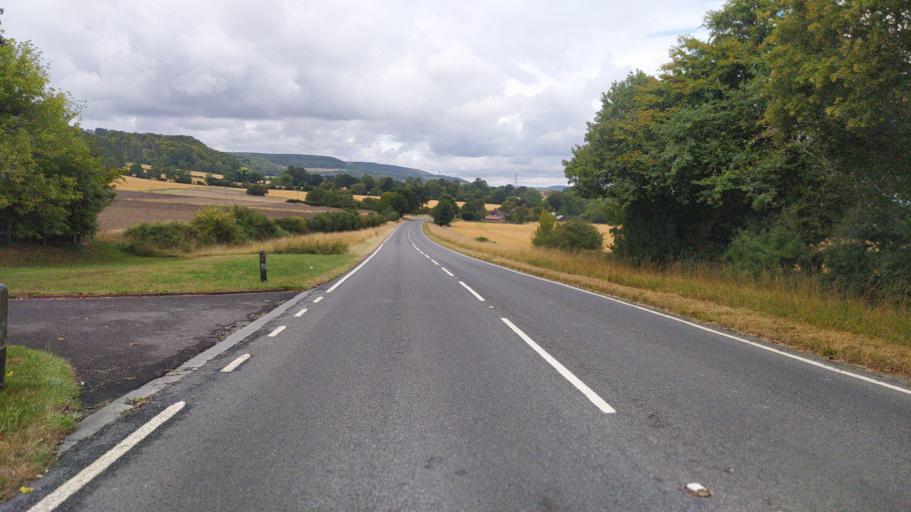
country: GB
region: England
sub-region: Hampshire
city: Petersfield
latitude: 50.9736
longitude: -0.9017
